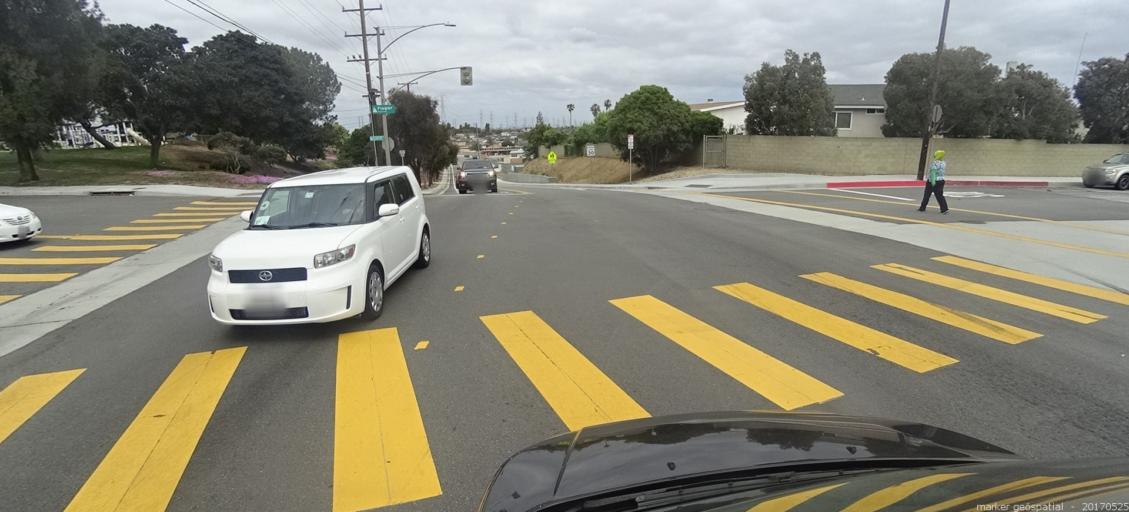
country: US
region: California
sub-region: Los Angeles County
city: Redondo Beach
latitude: 33.8550
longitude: -118.3785
